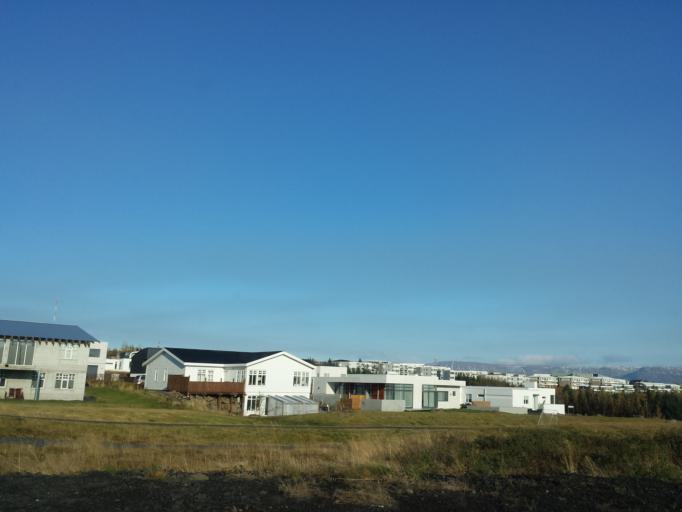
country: IS
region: Capital Region
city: Reykjavik
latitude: 64.0830
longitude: -21.8106
